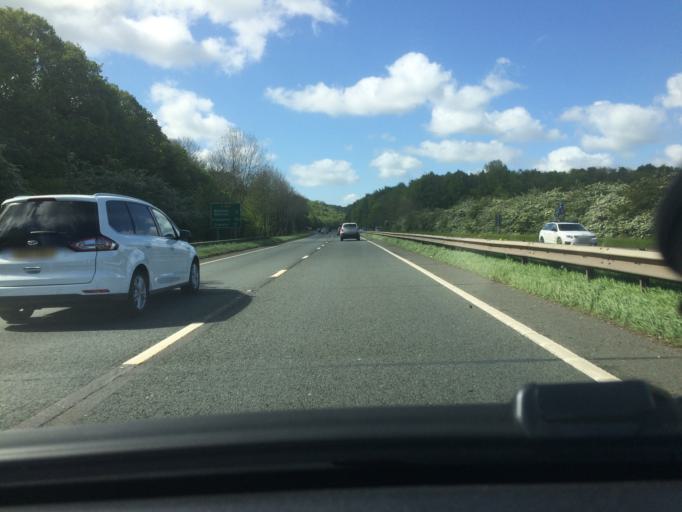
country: GB
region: Wales
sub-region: Wrexham
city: Gresford
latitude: 53.1007
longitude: -2.9621
